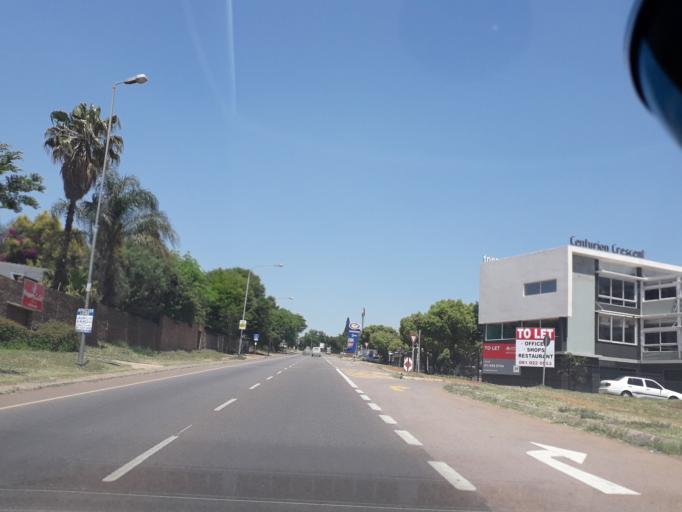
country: ZA
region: Gauteng
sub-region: City of Tshwane Metropolitan Municipality
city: Centurion
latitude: -25.8641
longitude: 28.1859
